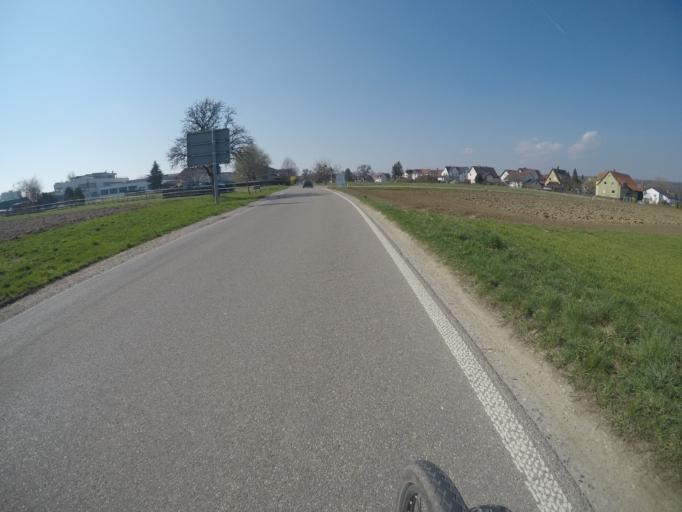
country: DE
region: Baden-Wuerttemberg
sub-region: Tuebingen Region
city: Kirchentellinsfurt
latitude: 48.5348
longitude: 9.1565
